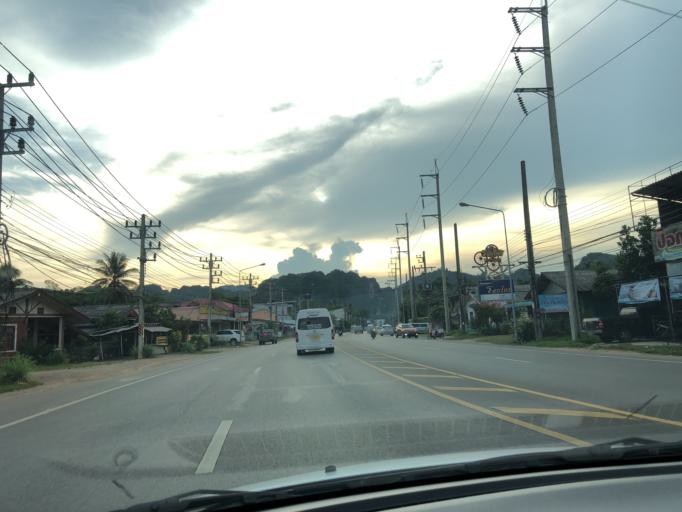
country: TH
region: Krabi
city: Krabi
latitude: 8.0849
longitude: 98.8862
